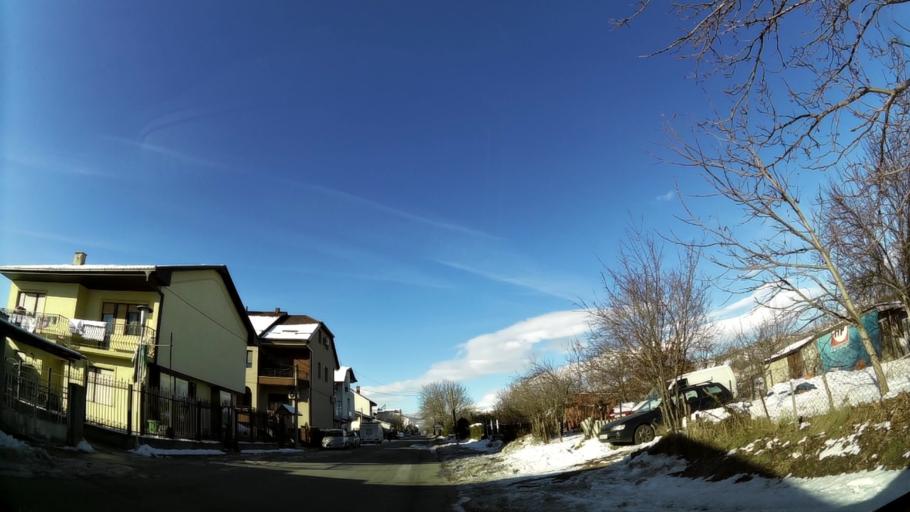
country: MK
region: Saraj
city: Saraj
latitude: 42.0100
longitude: 21.3378
